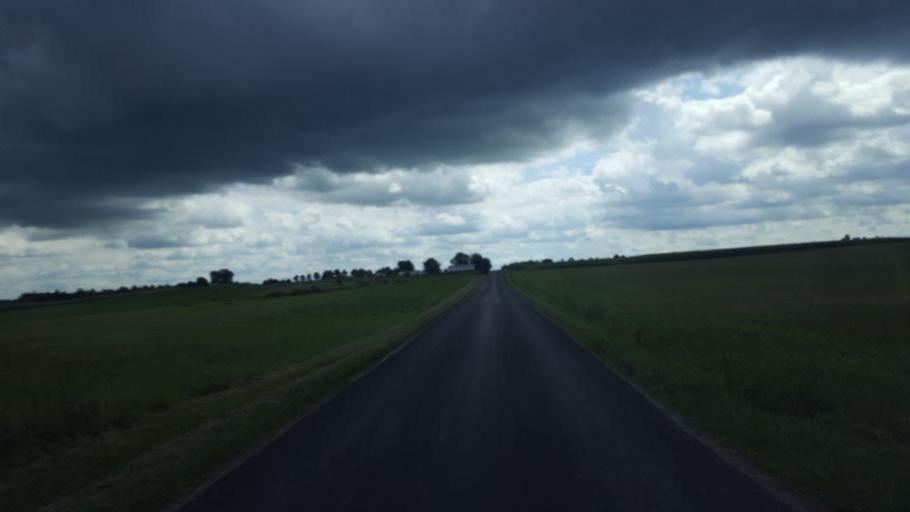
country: US
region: Ohio
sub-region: Huron County
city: Greenwich
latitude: 40.9810
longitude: -82.5347
